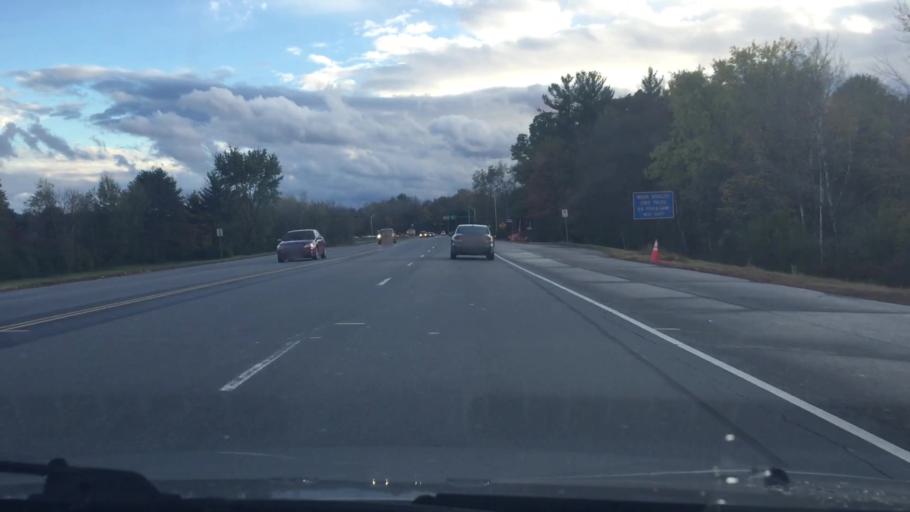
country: US
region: New Hampshire
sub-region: Cheshire County
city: Keene
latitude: 42.9273
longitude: -72.2991
